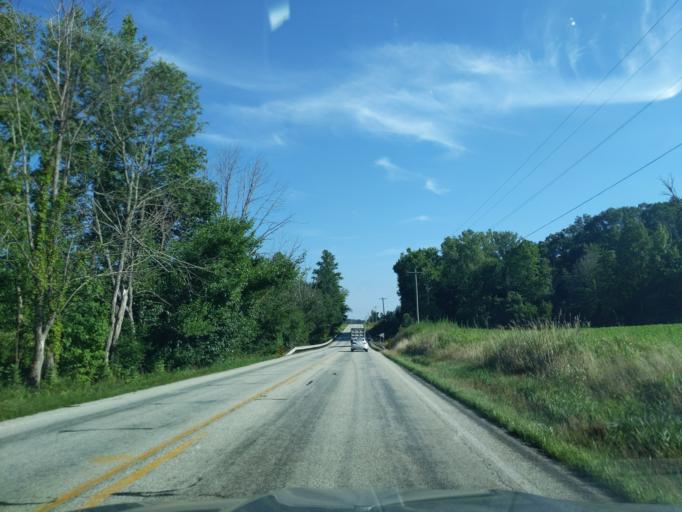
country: US
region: Indiana
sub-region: Ripley County
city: Versailles
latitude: 39.0869
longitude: -85.2748
